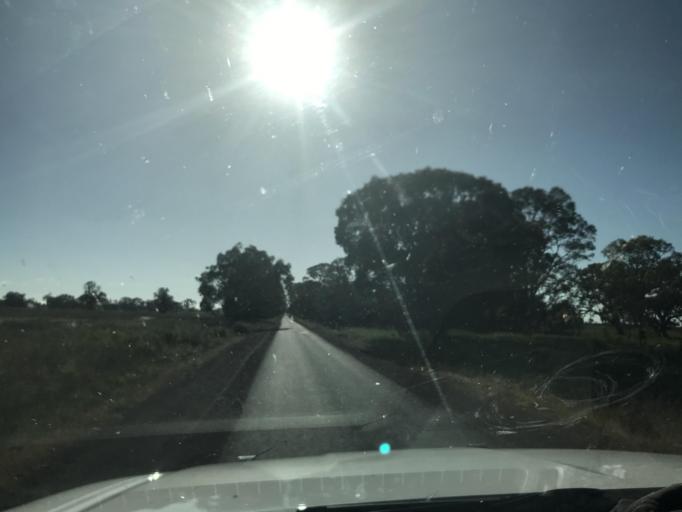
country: AU
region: Victoria
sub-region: Horsham
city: Horsham
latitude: -37.0054
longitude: 141.6245
